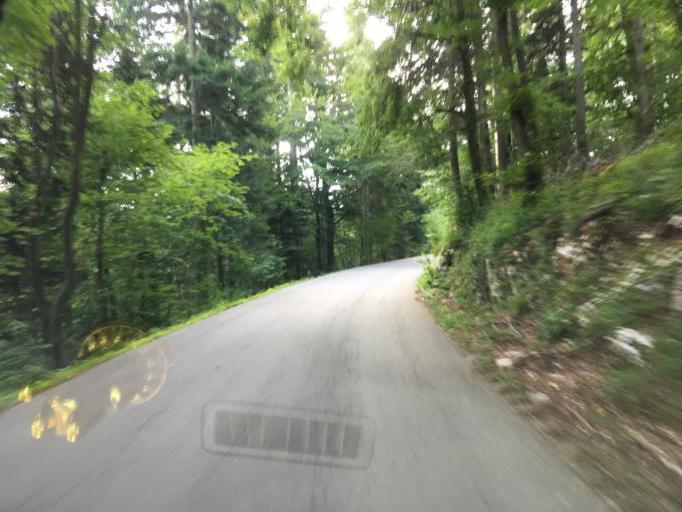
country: SI
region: Postojna
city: Postojna
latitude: 45.7992
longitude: 14.2006
